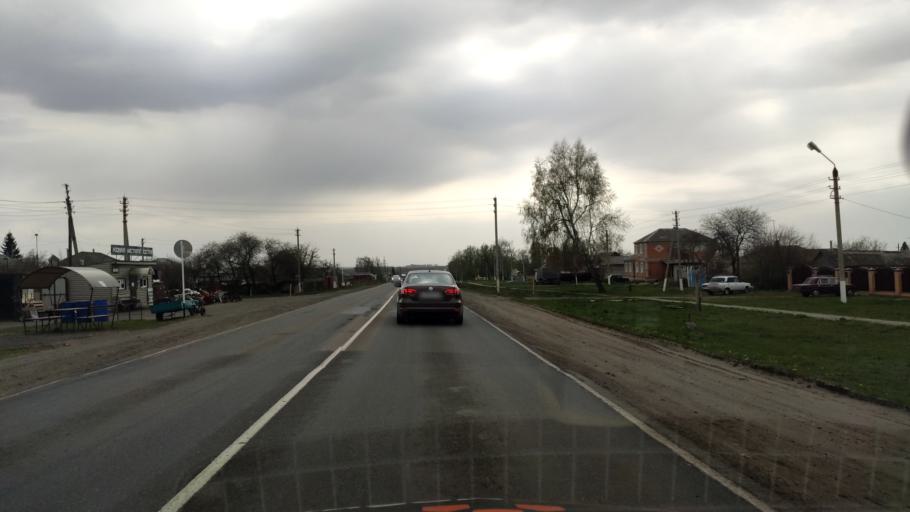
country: RU
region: Kursk
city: Gorshechnoye
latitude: 51.5210
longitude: 38.0194
